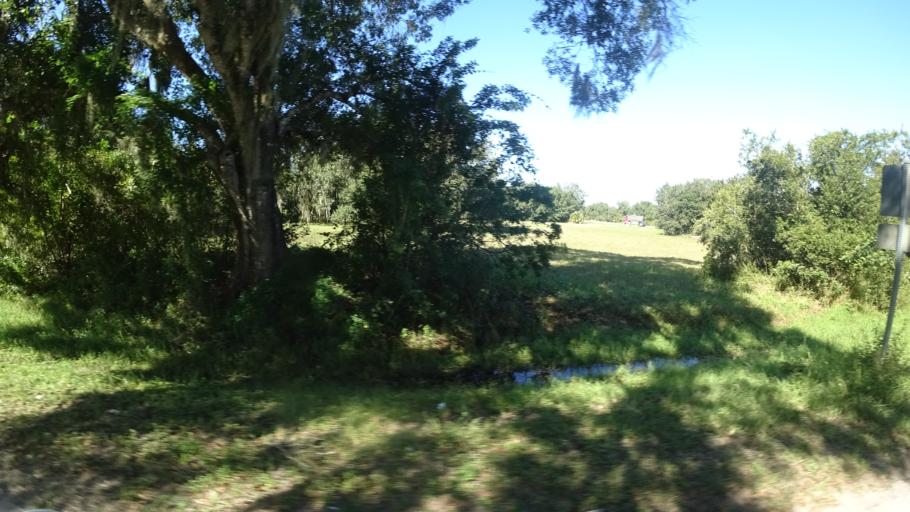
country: US
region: Florida
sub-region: Sarasota County
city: Lake Sarasota
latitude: 27.3867
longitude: -82.2682
